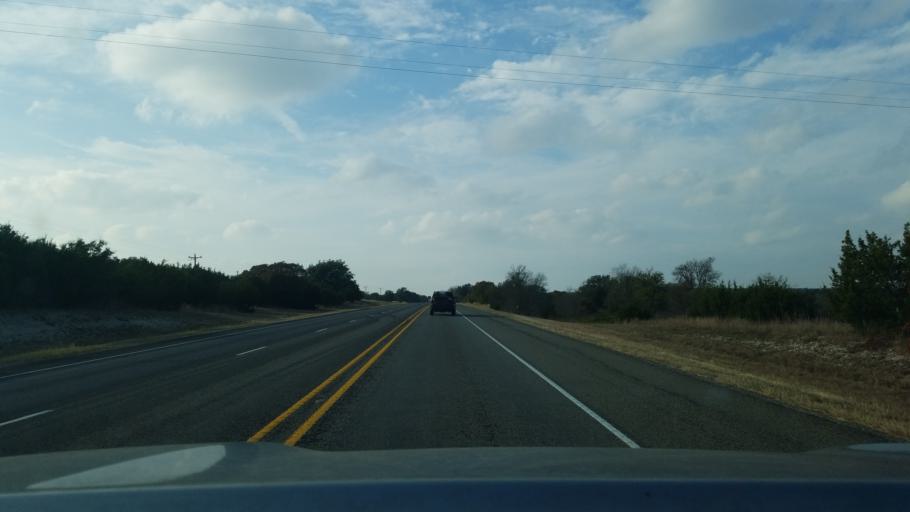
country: US
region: Texas
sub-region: Lampasas County
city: Lampasas
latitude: 31.1789
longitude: -98.3584
